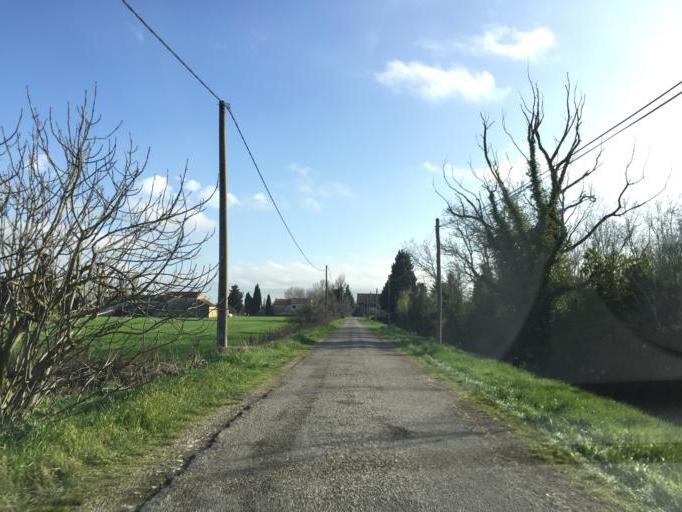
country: FR
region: Provence-Alpes-Cote d'Azur
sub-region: Departement du Vaucluse
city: Orange
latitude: 44.1393
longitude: 4.8261
